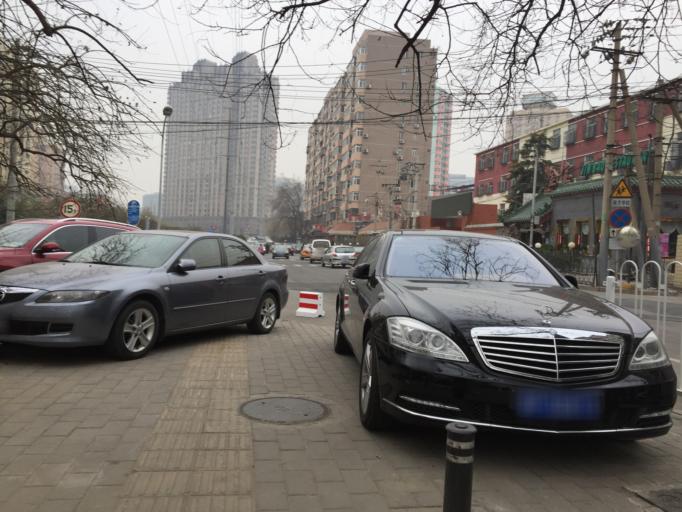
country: CN
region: Beijing
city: Chaowai
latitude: 39.9452
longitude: 116.4411
